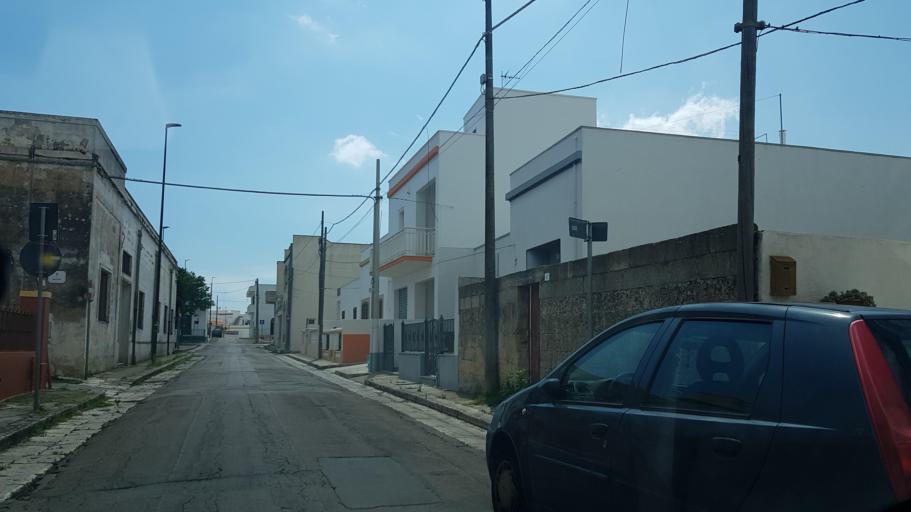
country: IT
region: Apulia
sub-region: Provincia di Lecce
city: Castrignano del Capo
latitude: 39.8324
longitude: 18.3531
